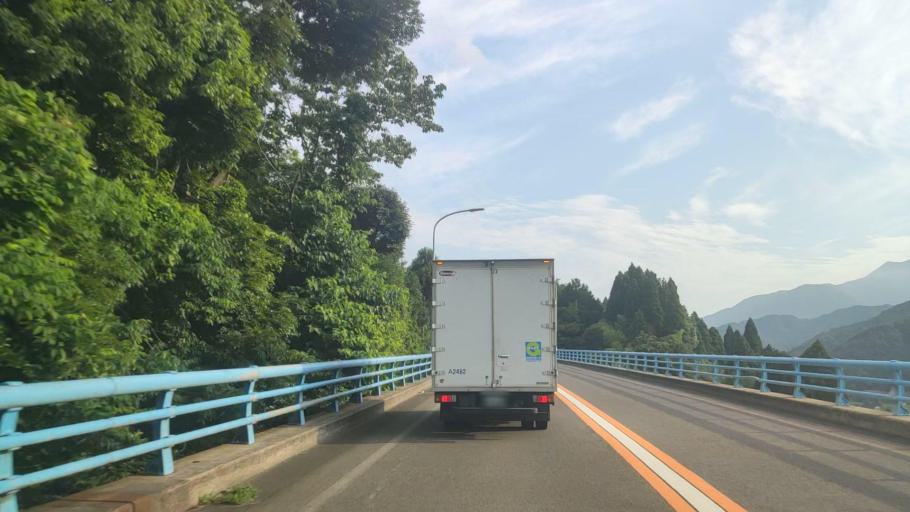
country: JP
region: Tottori
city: Kurayoshi
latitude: 35.3548
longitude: 133.7506
